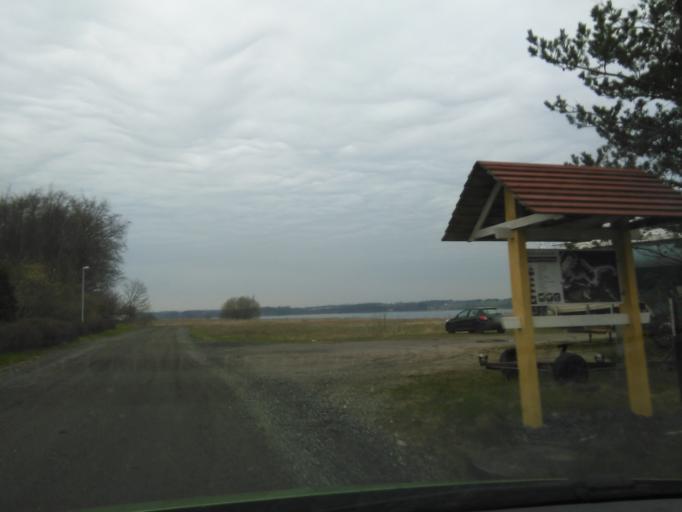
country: DK
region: North Denmark
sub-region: Mariagerfjord Kommune
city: Hadsund
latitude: 56.6841
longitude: 10.0699
